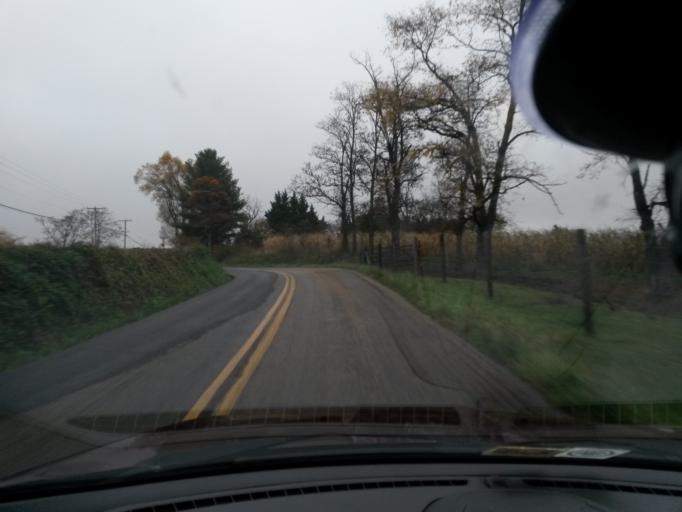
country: US
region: Virginia
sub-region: Botetourt County
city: Fincastle
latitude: 37.4609
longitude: -79.8422
